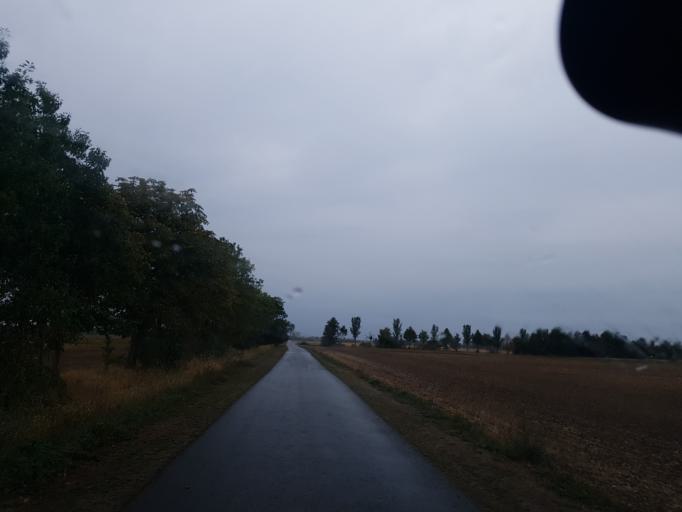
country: DE
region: Saxony-Anhalt
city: Jessen
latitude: 51.7711
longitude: 12.8980
